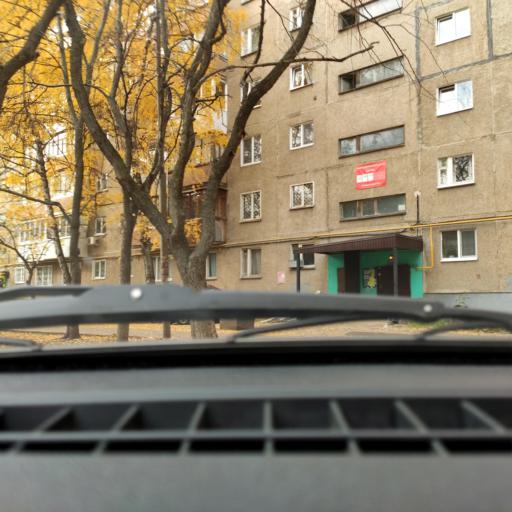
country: RU
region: Bashkortostan
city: Ufa
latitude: 54.7443
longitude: 56.0209
